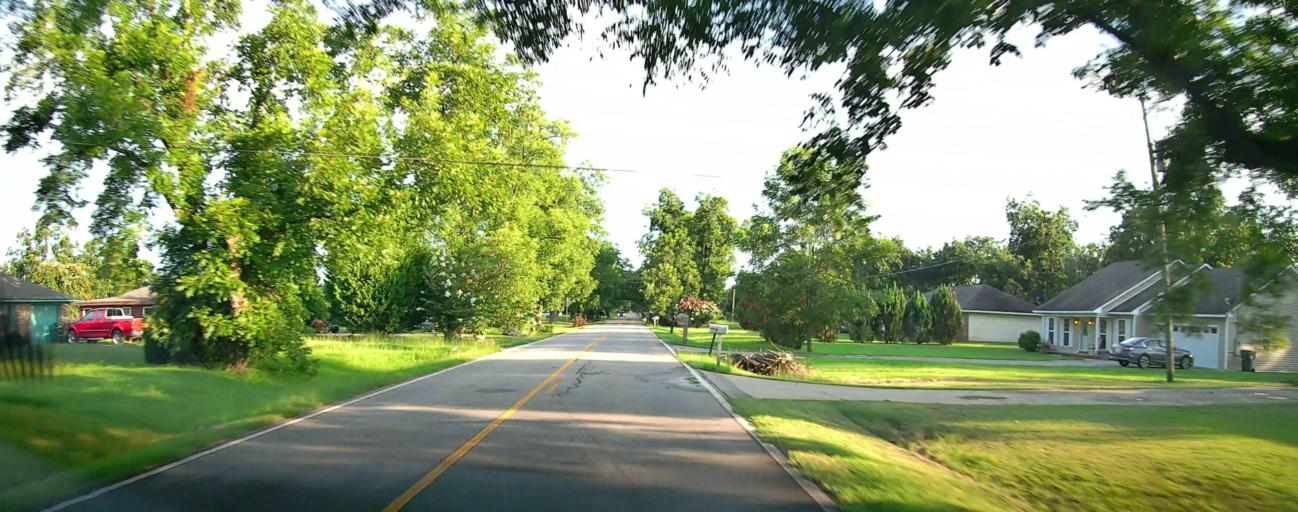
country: US
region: Georgia
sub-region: Peach County
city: Fort Valley
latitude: 32.5860
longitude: -83.8739
